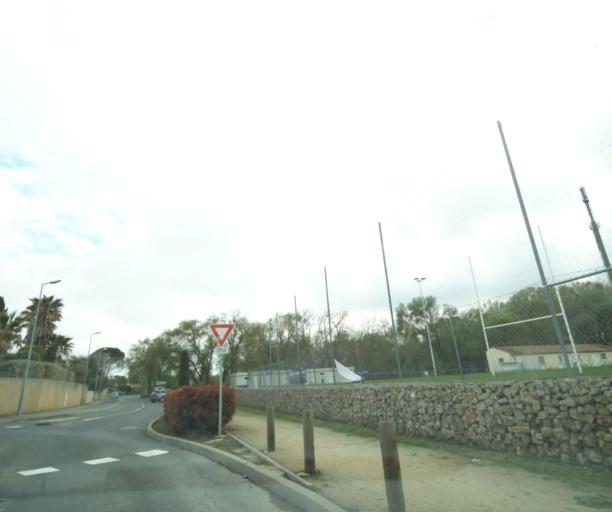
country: FR
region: Languedoc-Roussillon
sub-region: Departement de l'Herault
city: Saint-Jean-de-Vedas
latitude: 43.5805
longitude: 3.8177
